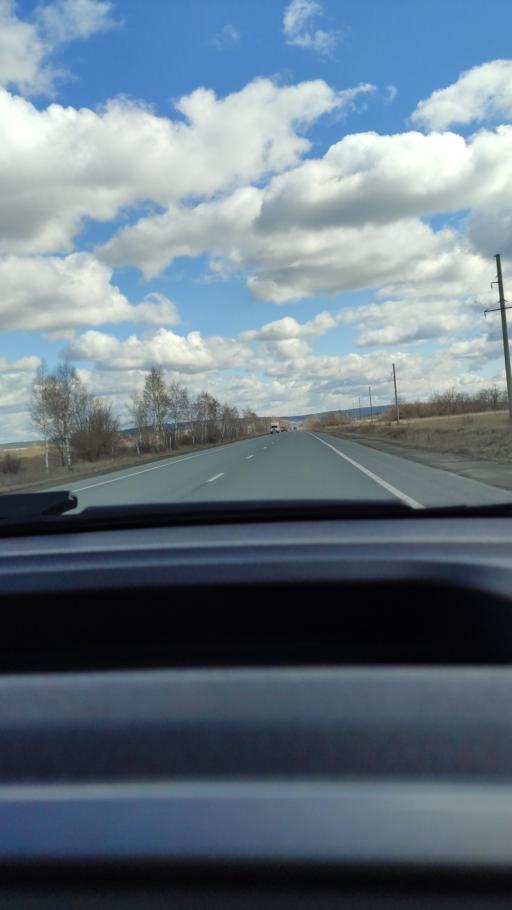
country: RU
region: Samara
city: Kurumoch
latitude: 53.4907
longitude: 49.9788
